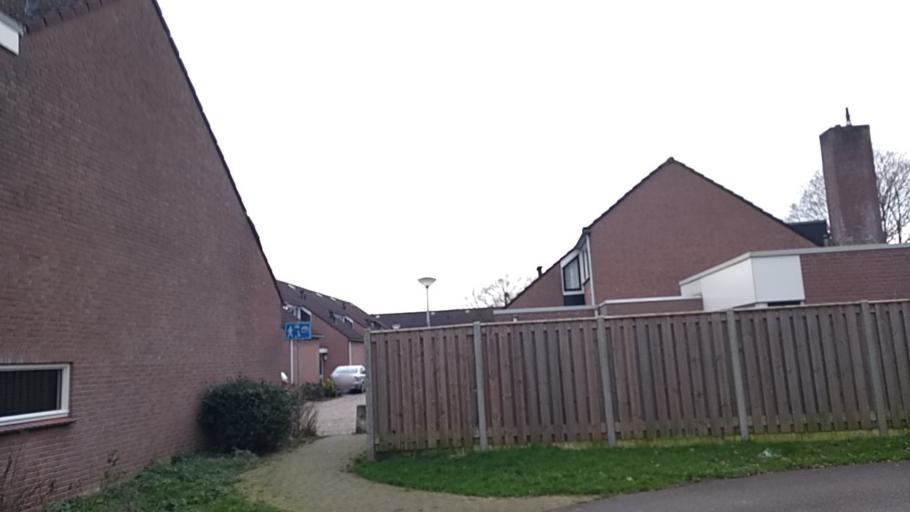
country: NL
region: Overijssel
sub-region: Gemeente Almelo
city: Almelo
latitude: 52.3780
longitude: 6.6855
